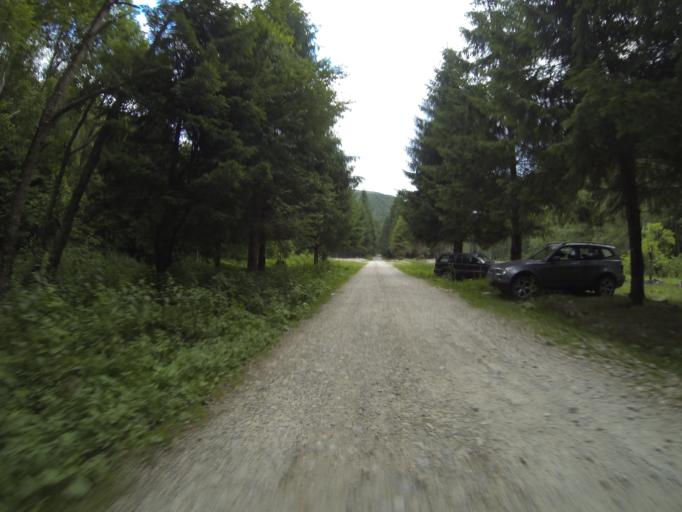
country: RO
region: Gorj
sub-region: Comuna Polovragi
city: Polovragi
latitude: 45.2671
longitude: 23.7709
